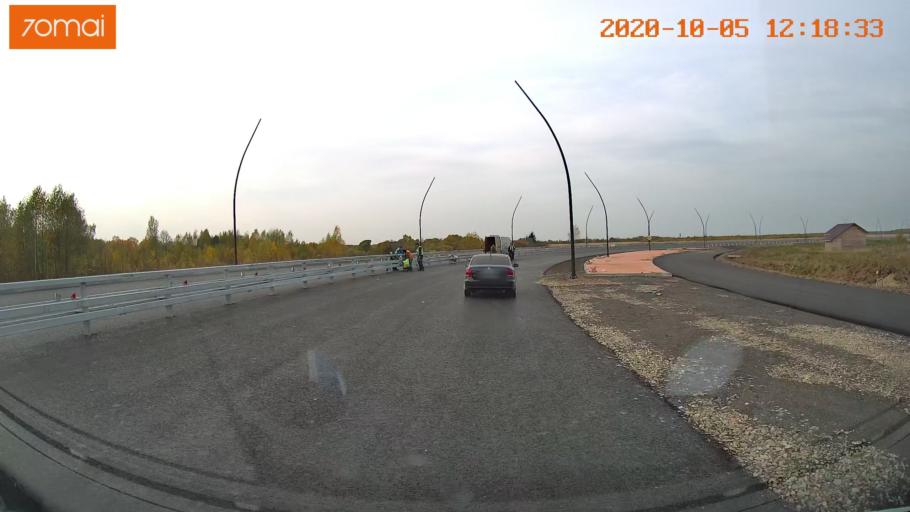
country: RU
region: Ivanovo
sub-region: Gorod Ivanovo
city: Ivanovo
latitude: 56.9512
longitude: 40.9405
